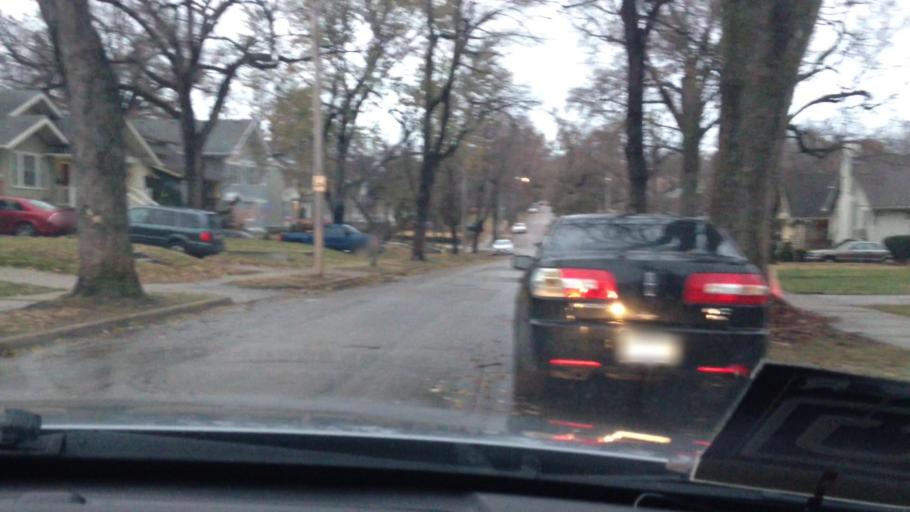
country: US
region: Kansas
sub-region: Johnson County
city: Mission Hills
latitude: 39.0263
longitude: -94.5751
